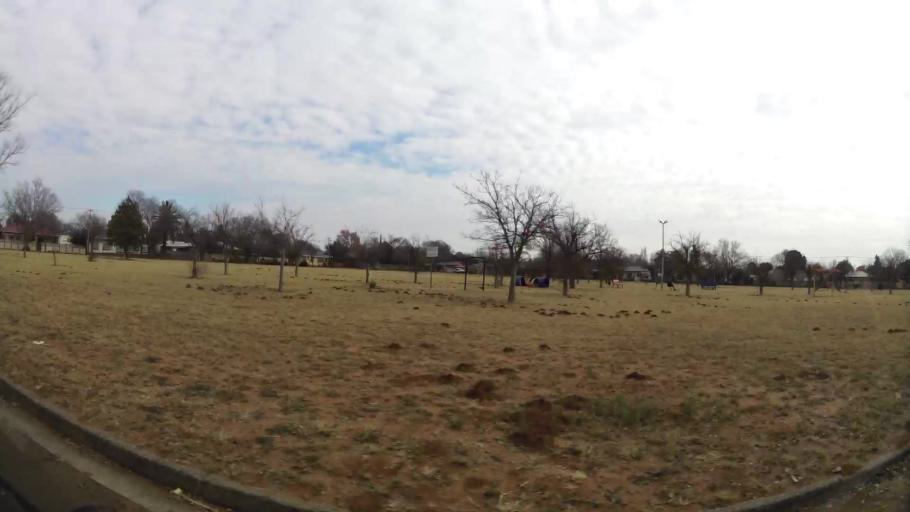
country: ZA
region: Orange Free State
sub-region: Mangaung Metropolitan Municipality
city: Bloemfontein
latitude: -29.1283
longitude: 26.1798
